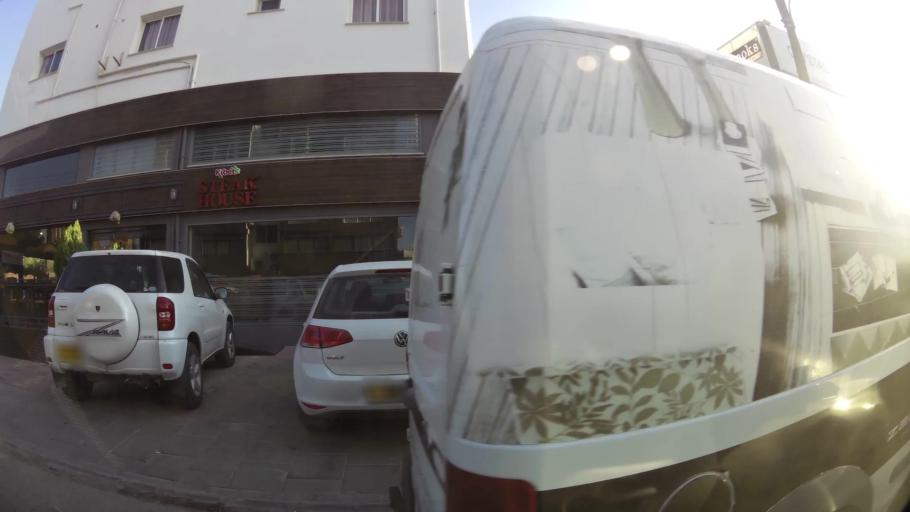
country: CY
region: Lefkosia
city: Nicosia
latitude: 35.1895
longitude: 33.3577
